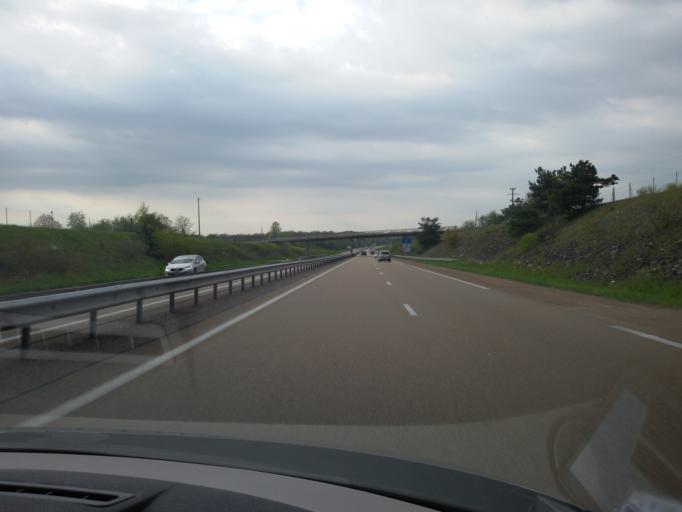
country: FR
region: Champagne-Ardenne
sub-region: Departement de la Haute-Marne
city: Chamarandes-Choignes
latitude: 47.9771
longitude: 5.1361
